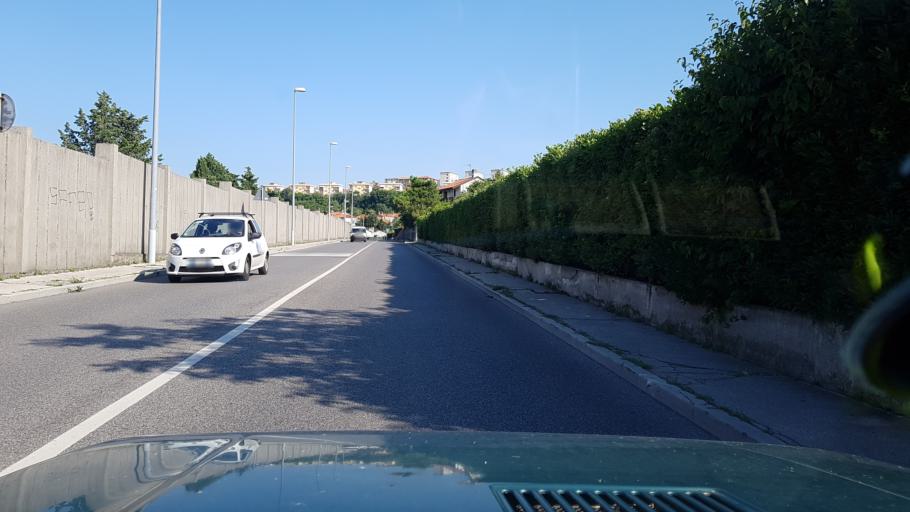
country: IT
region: Friuli Venezia Giulia
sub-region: Provincia di Trieste
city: Trieste
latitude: 45.6308
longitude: 13.7979
